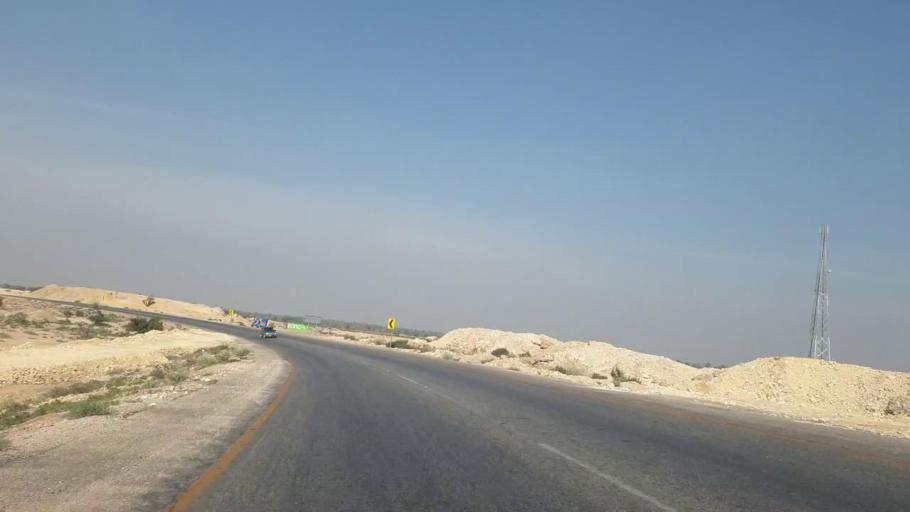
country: PK
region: Sindh
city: Hala
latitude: 25.8631
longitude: 68.2600
